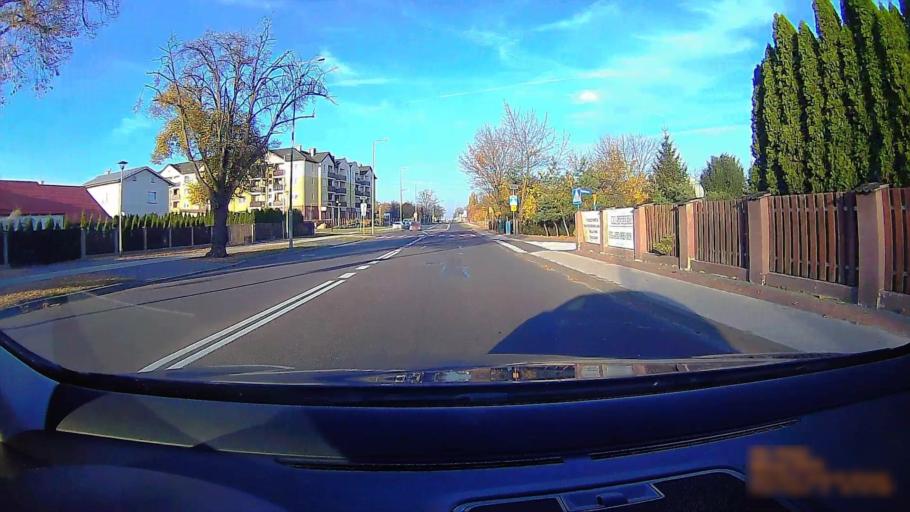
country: PL
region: Greater Poland Voivodeship
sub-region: Powiat koninski
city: Stare Miasto
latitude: 52.1931
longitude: 18.2354
